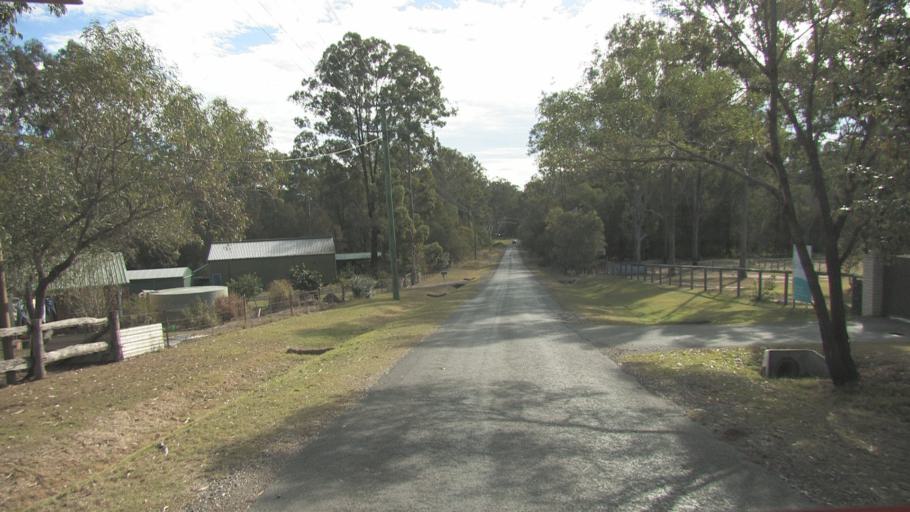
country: AU
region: Queensland
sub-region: Logan
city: Cedar Vale
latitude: -27.8280
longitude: 153.0694
